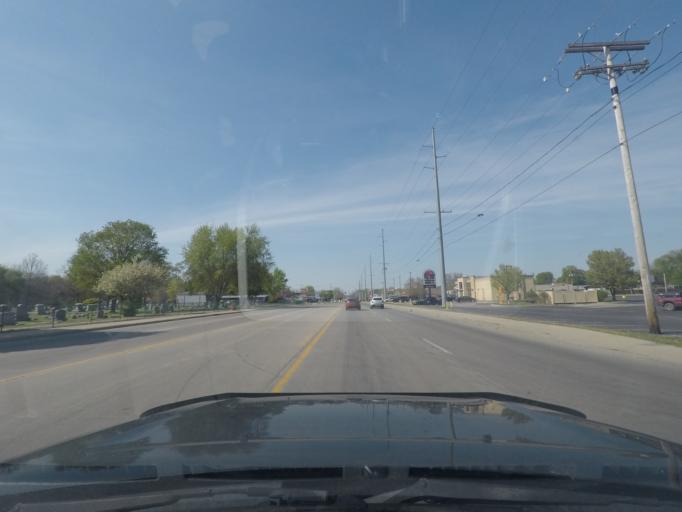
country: US
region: Indiana
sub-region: Elkhart County
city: Elkhart
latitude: 41.6720
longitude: -86.0032
